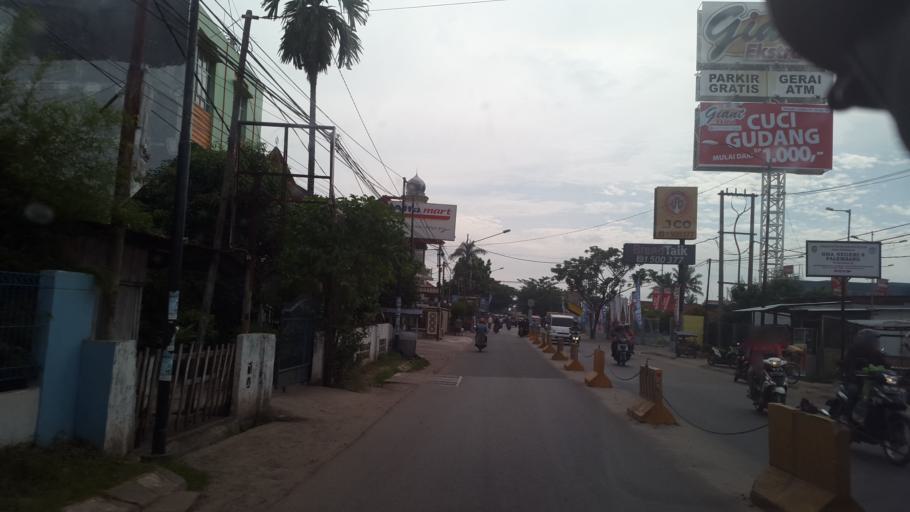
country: ID
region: South Sumatra
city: Plaju
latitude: -2.9920
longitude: 104.7962
